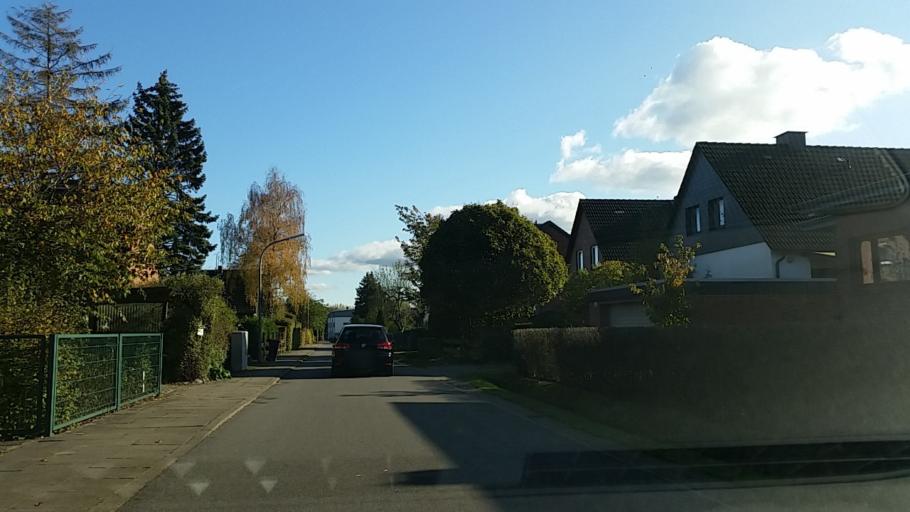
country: DE
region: Hamburg
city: Wandsbek
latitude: 53.5495
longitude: 10.1127
